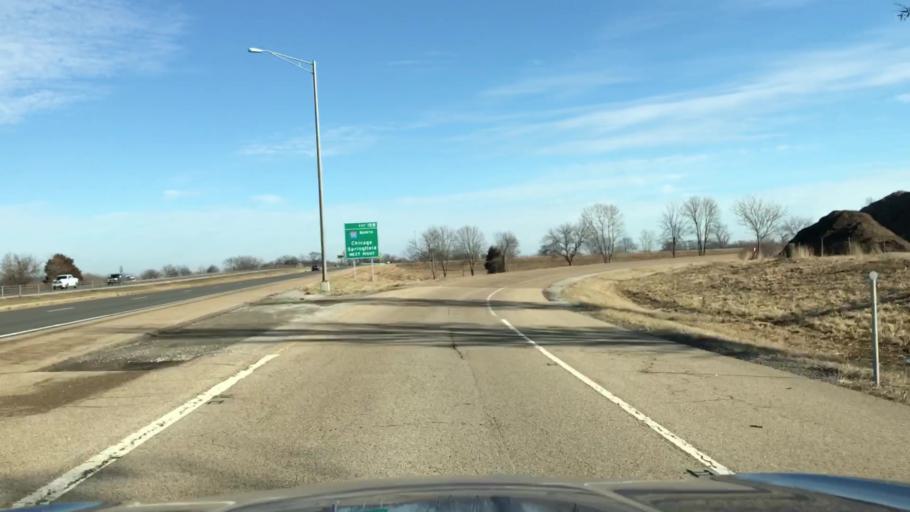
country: US
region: Illinois
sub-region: Madison County
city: Troy
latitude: 38.7519
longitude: -89.9126
